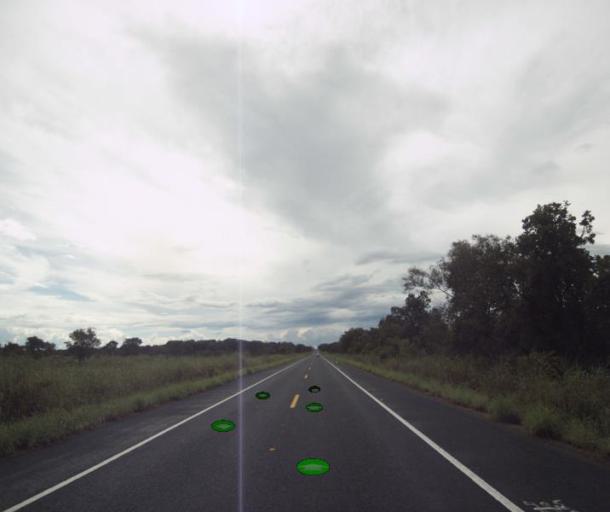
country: BR
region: Goias
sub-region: Sao Miguel Do Araguaia
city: Sao Miguel do Araguaia
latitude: -13.2613
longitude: -50.5172
